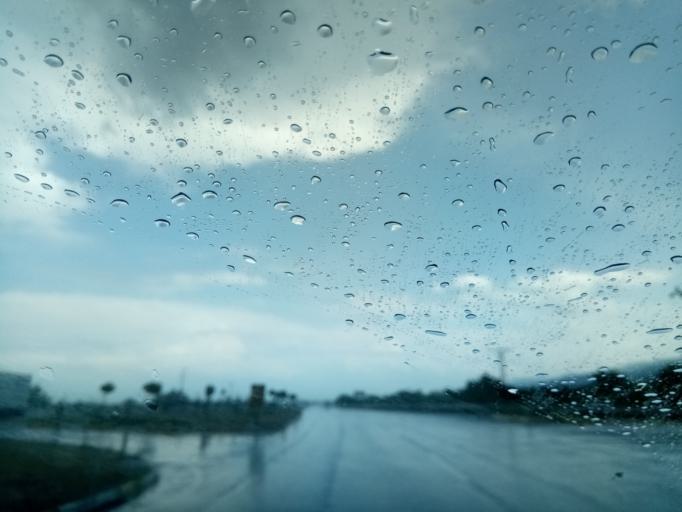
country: TR
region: Afyonkarahisar
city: Sultandagi
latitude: 38.4852
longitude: 31.2796
